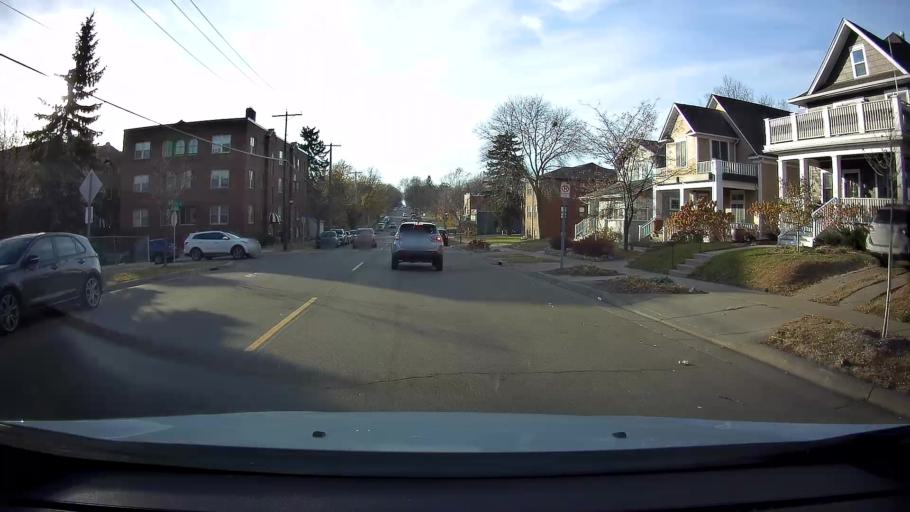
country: US
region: Minnesota
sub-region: Dakota County
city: West Saint Paul
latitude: 44.9342
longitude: -93.1374
